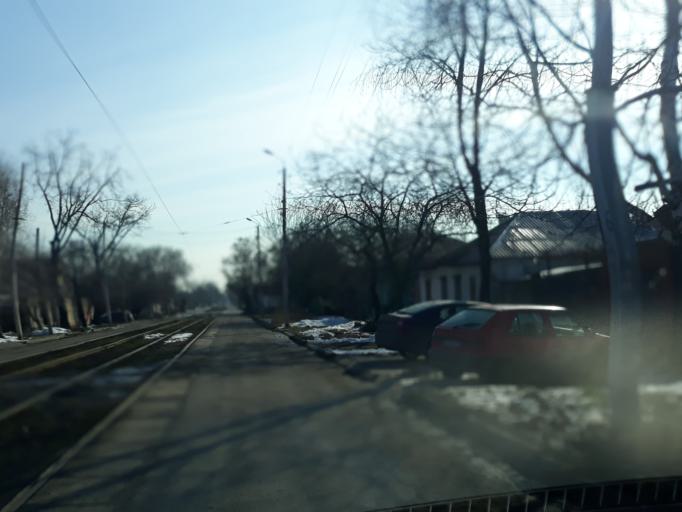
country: RU
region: Rostov
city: Taganrog
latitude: 47.2087
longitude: 38.9109
